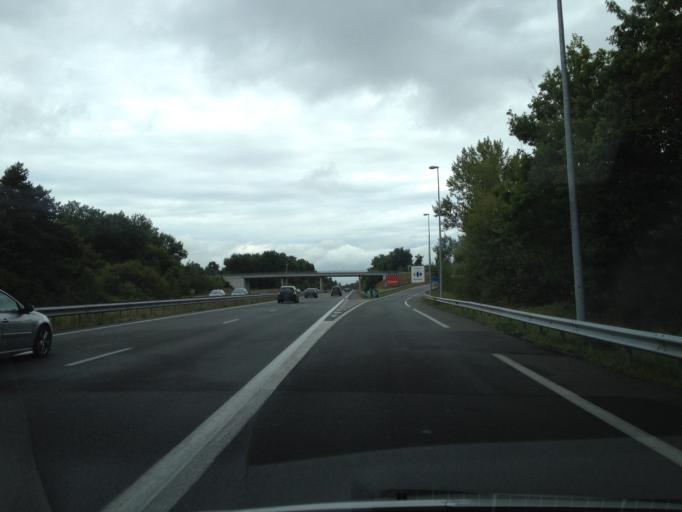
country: FR
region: Aquitaine
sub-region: Departement du Lot-et-Garonne
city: Fourques-sur-Garonne
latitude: 44.4018
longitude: 0.1884
